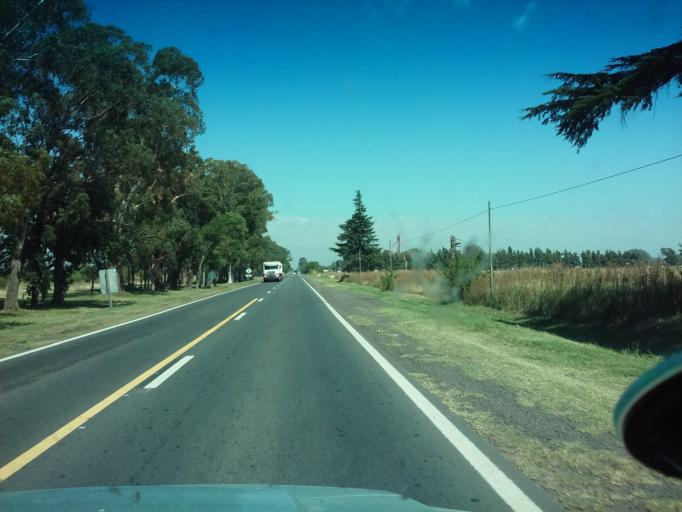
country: AR
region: Buenos Aires
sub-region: Partido de Nueve de Julio
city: Nueve de Julio
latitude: -35.4823
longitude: -60.8771
